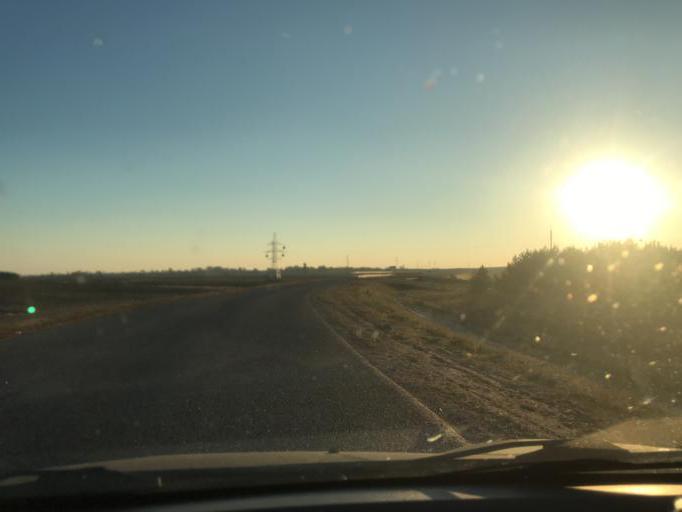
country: BY
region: Gomel
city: Brahin
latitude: 51.8454
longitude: 30.3486
